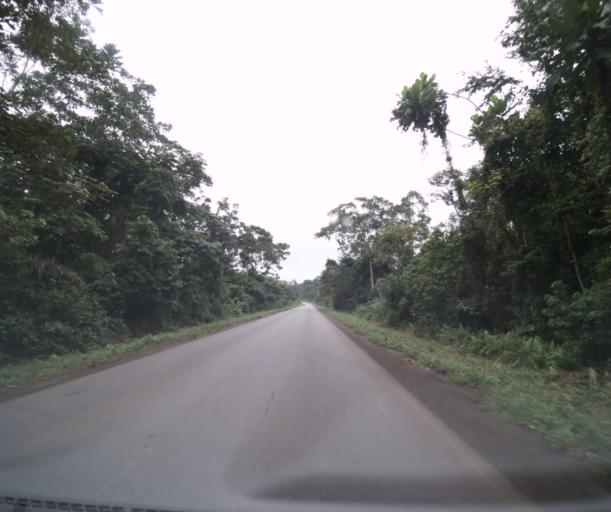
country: CM
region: Littoral
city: Edea
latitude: 3.6709
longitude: 10.1108
